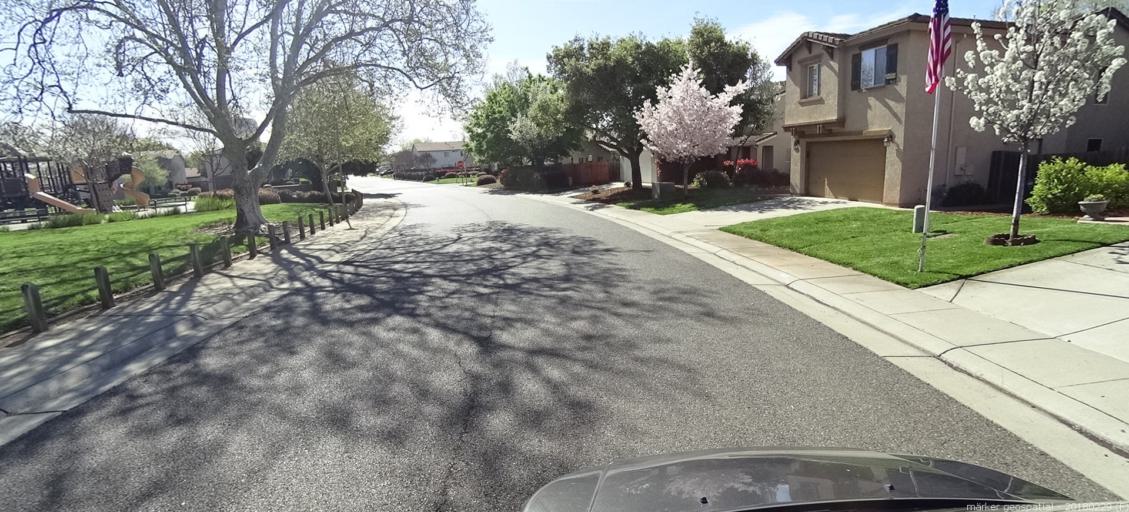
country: US
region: California
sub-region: Sacramento County
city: Rancho Cordova
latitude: 38.5456
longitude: -121.2838
